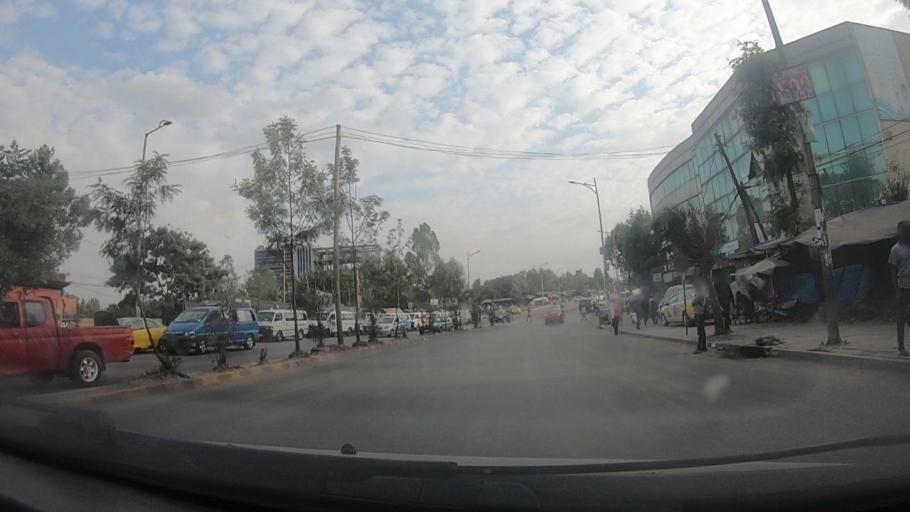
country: ET
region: Adis Abeba
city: Addis Ababa
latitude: 8.9657
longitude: 38.7328
